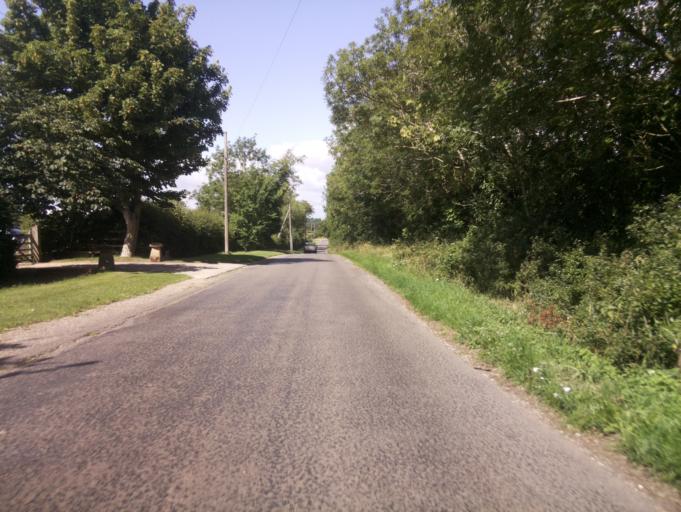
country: GB
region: England
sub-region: Buckinghamshire
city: Winslow
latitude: 51.9942
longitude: -0.8971
